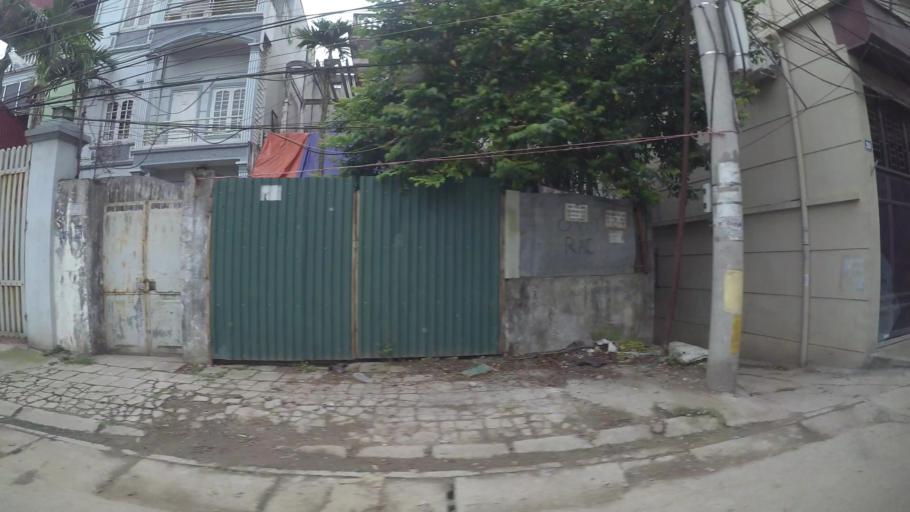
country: VN
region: Ha Noi
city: Tay Ho
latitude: 21.0665
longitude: 105.8356
